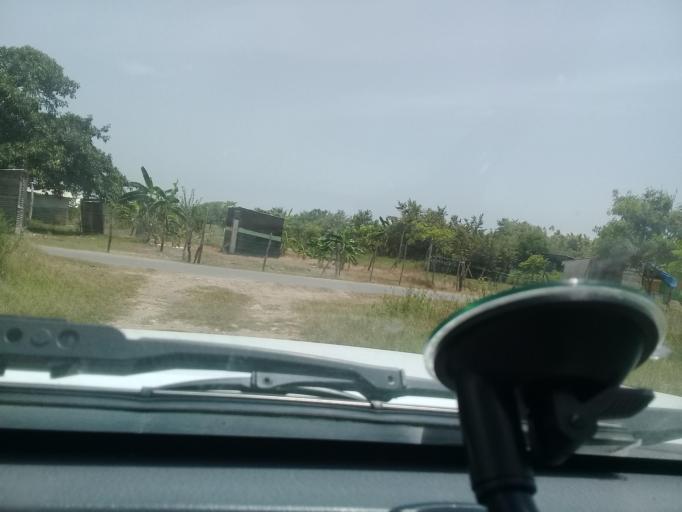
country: MX
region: Veracruz
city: Anahuac
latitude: 22.2229
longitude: -97.8263
